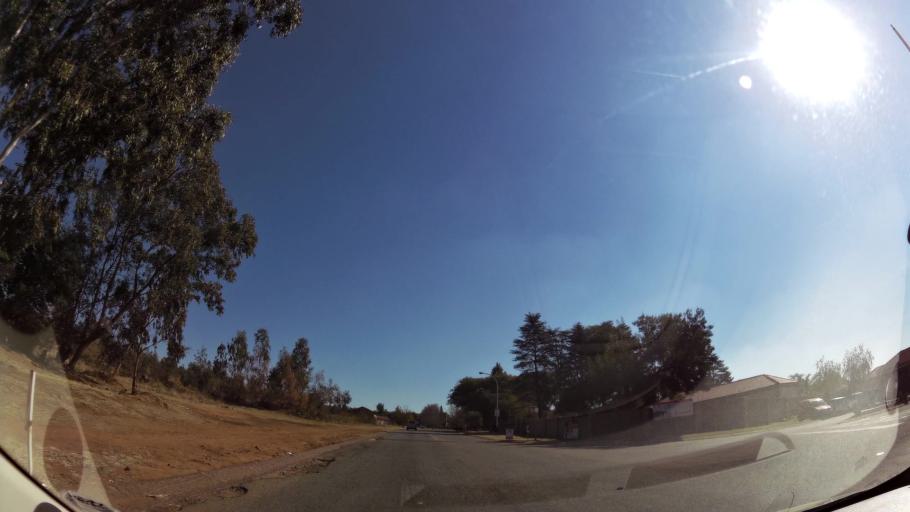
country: ZA
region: Mpumalanga
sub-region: Nkangala District Municipality
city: Witbank
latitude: -25.8354
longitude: 29.2455
